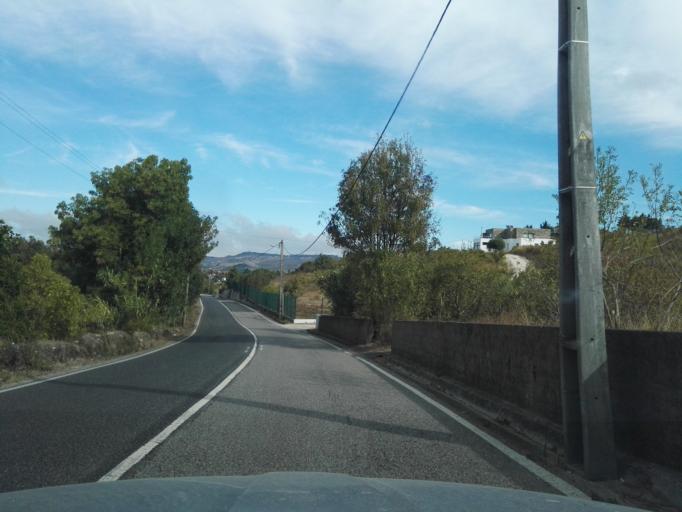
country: PT
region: Lisbon
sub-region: Arruda Dos Vinhos
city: Arruda dos Vinhos
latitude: 38.9671
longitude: -9.0641
